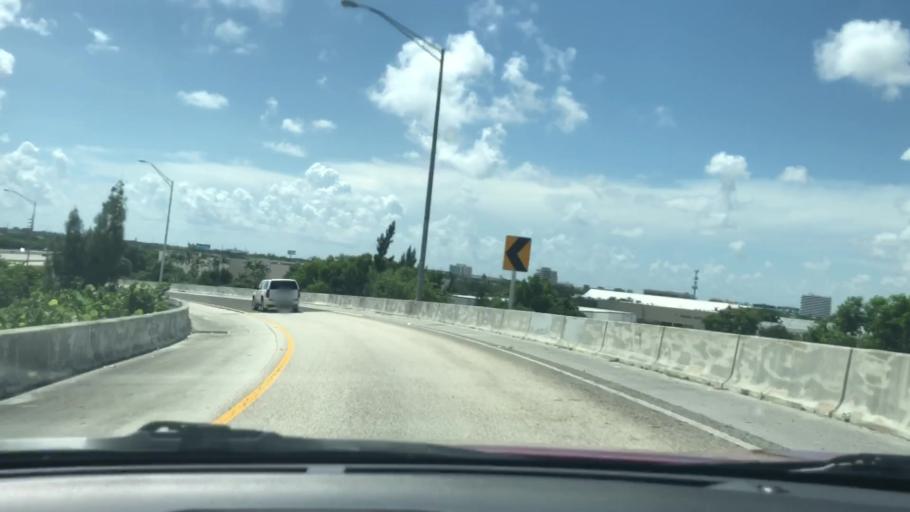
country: US
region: Florida
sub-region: Palm Beach County
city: West Palm Beach
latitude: 26.7057
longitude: -80.0774
